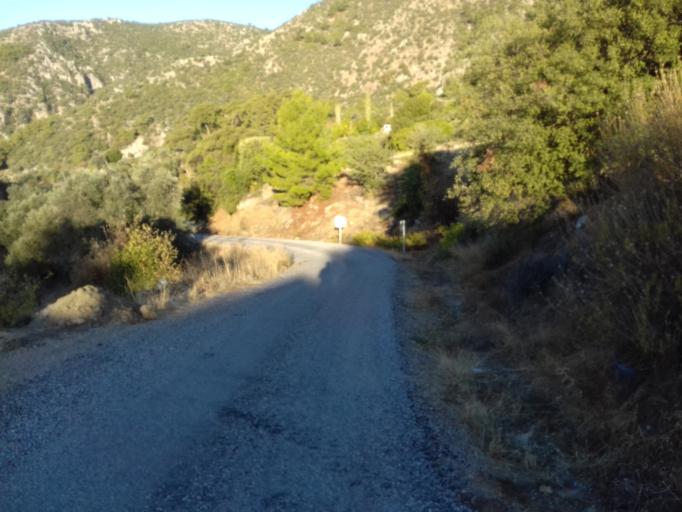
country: TR
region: Mugla
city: Yaniklar
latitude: 36.7863
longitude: 29.0234
